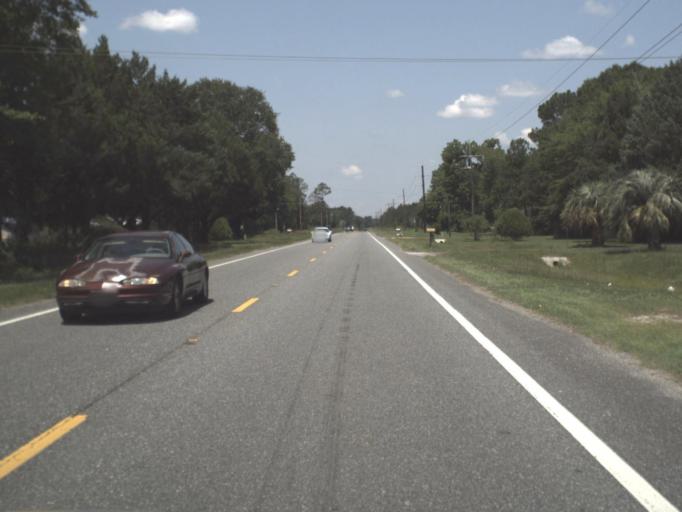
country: US
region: Florida
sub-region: Bradford County
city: Starke
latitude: 29.9643
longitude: -82.1845
